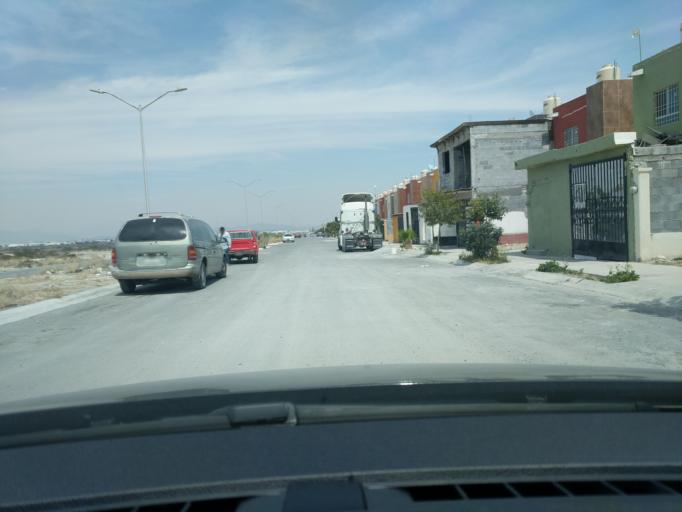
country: MX
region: Coahuila
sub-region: Arteaga
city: Arteaga
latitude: 25.4213
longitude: -100.9112
